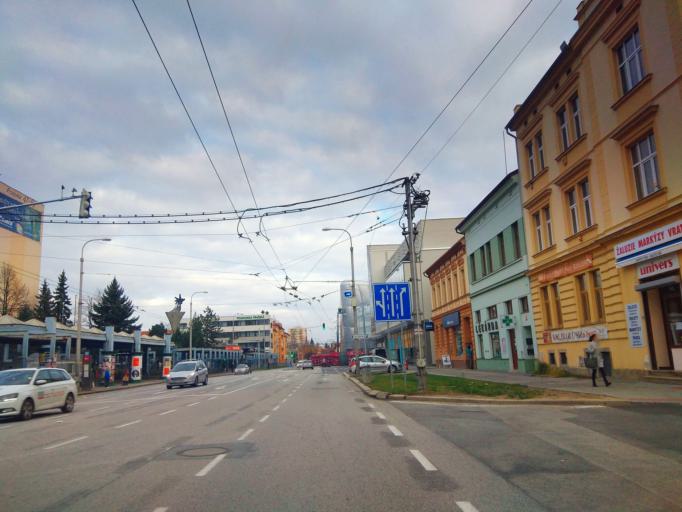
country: CZ
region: Jihocesky
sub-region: Okres Ceske Budejovice
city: Ceske Budejovice
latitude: 48.9826
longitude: 14.4717
